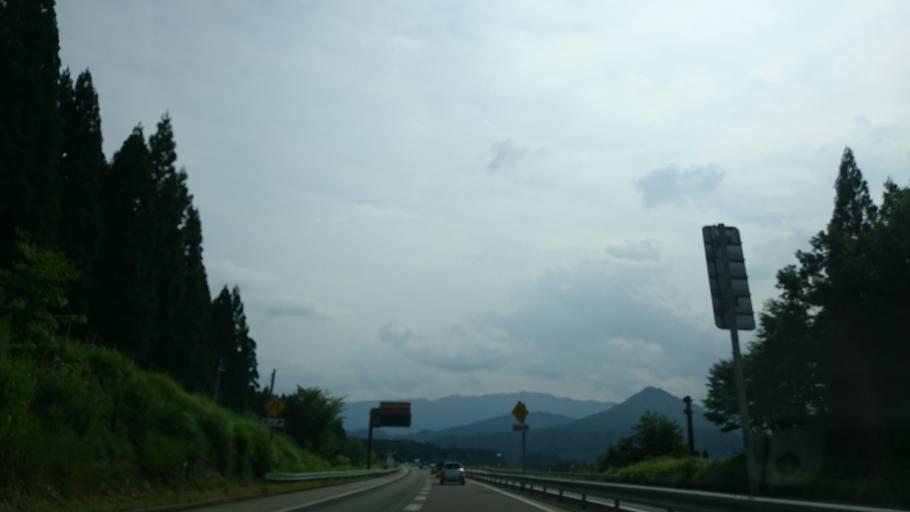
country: JP
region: Gifu
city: Gujo
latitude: 35.9407
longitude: 136.8853
